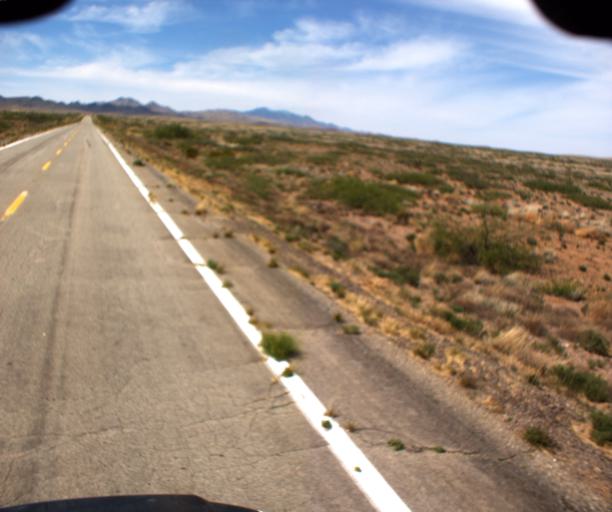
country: US
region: Arizona
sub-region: Cochise County
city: Willcox
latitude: 32.3785
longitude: -109.6464
